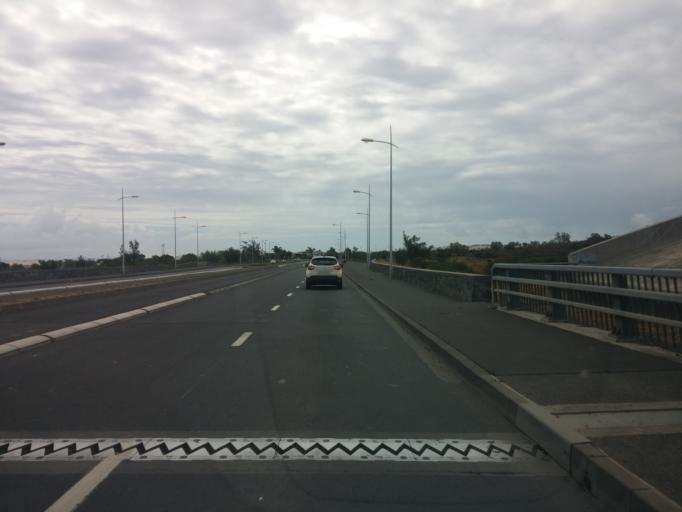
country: RE
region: Reunion
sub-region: Reunion
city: Le Port
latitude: -20.9564
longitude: 55.2943
